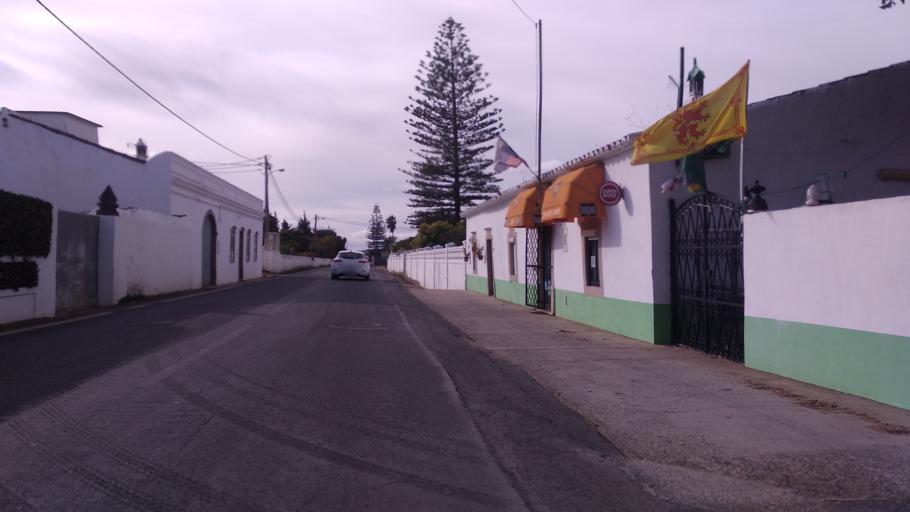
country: PT
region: Faro
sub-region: Sao Bras de Alportel
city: Sao Bras de Alportel
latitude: 37.1525
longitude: -7.9142
